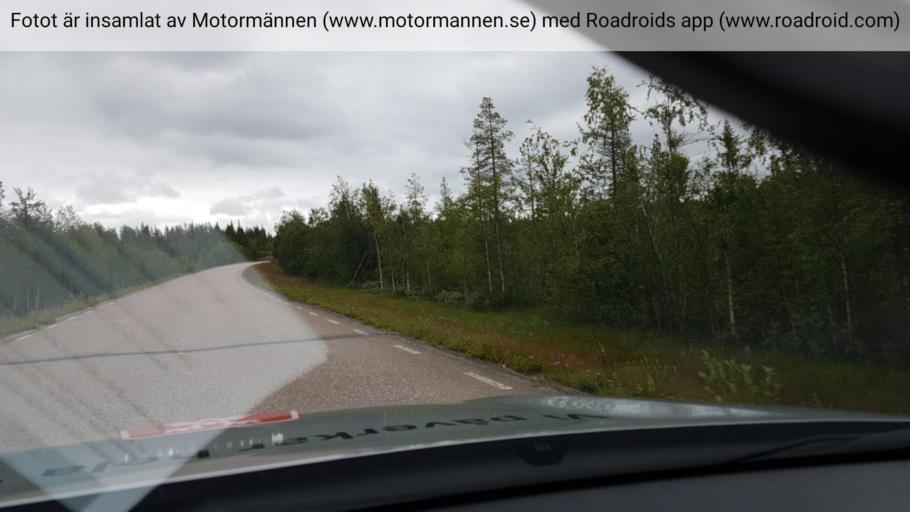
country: SE
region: Norrbotten
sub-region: Overkalix Kommun
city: OEverkalix
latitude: 67.0441
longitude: 22.0519
